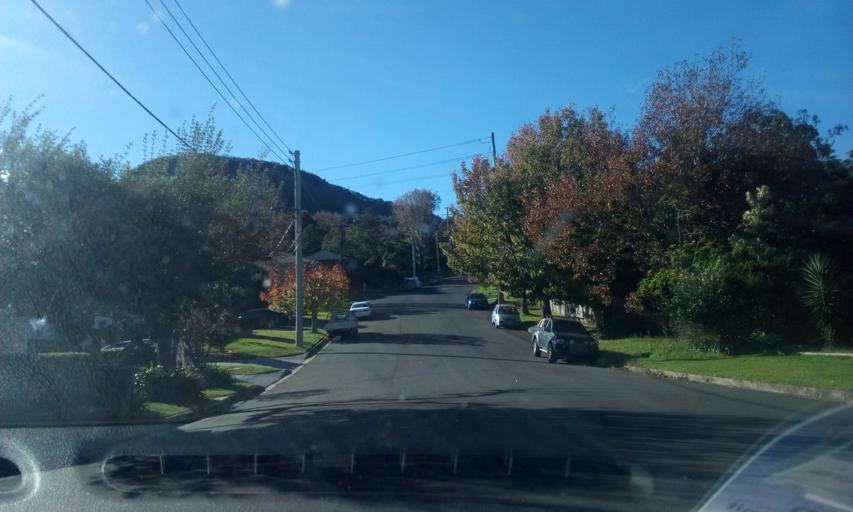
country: AU
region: New South Wales
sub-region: Wollongong
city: Mount Keira
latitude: -34.4159
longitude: 150.8568
